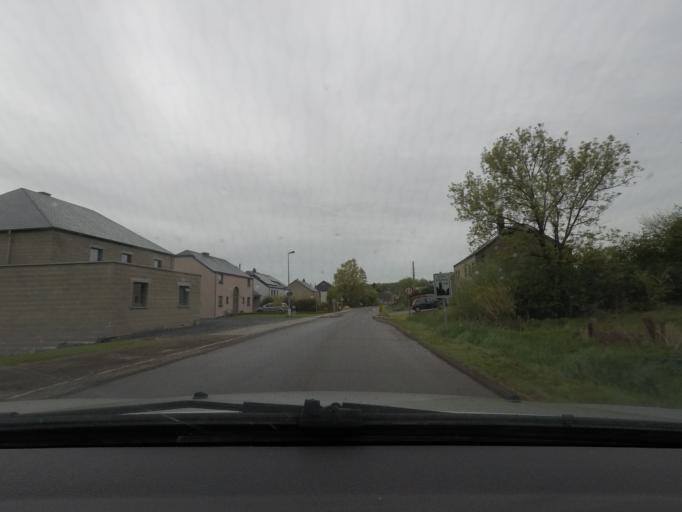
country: BE
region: Wallonia
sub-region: Province du Luxembourg
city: Etalle
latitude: 49.6945
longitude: 5.5609
